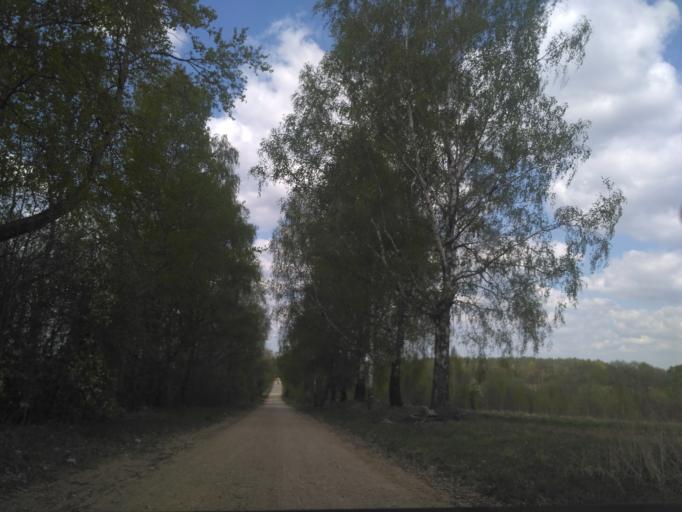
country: BY
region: Minsk
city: Il'ya
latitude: 54.2789
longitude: 27.3051
